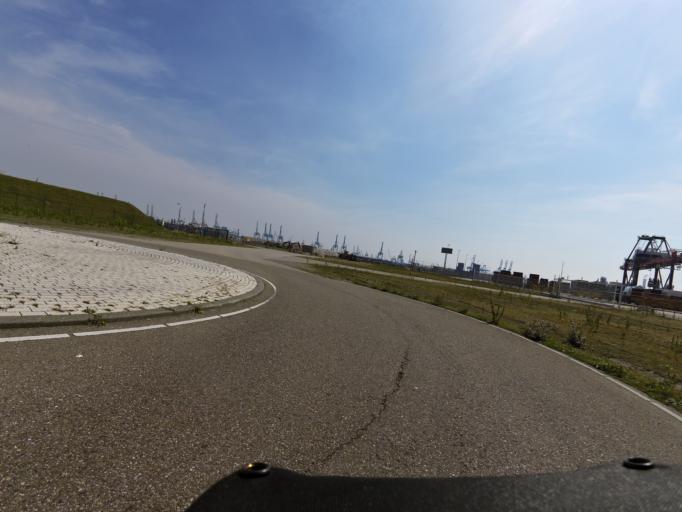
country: NL
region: South Holland
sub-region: Gemeente Rotterdam
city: Hoek van Holland
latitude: 51.9750
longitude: 4.0466
